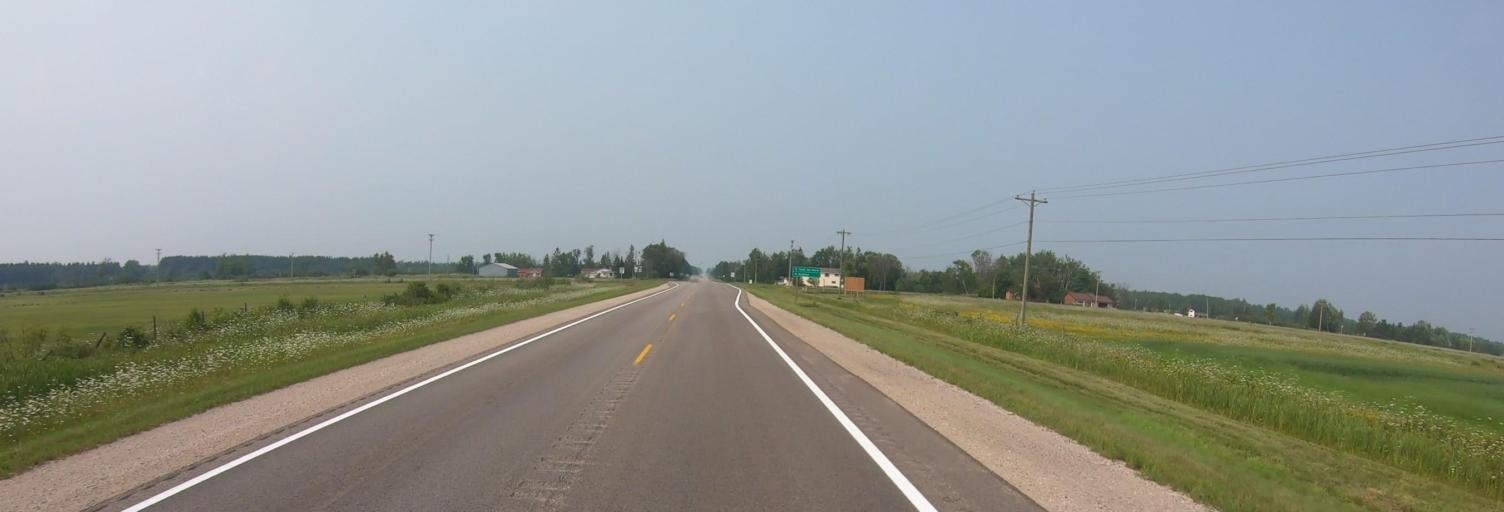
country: US
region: Michigan
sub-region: Chippewa County
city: Sault Ste. Marie
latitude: 46.1851
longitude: -84.3635
